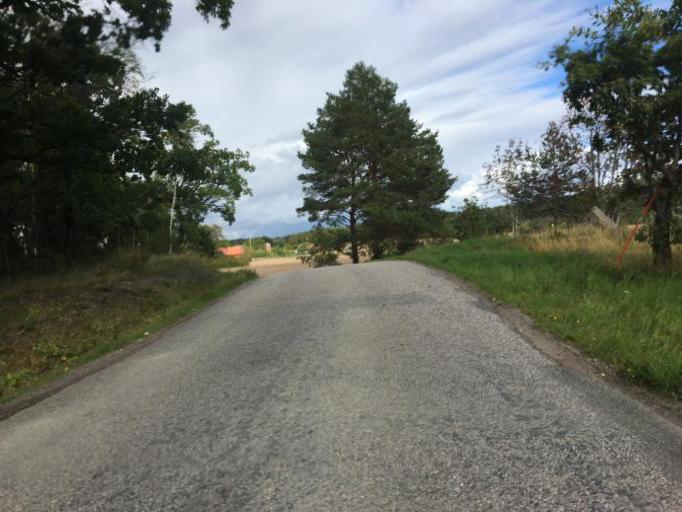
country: SE
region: Soedermanland
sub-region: Eskilstuna Kommun
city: Eskilstuna
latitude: 59.4449
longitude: 16.6407
